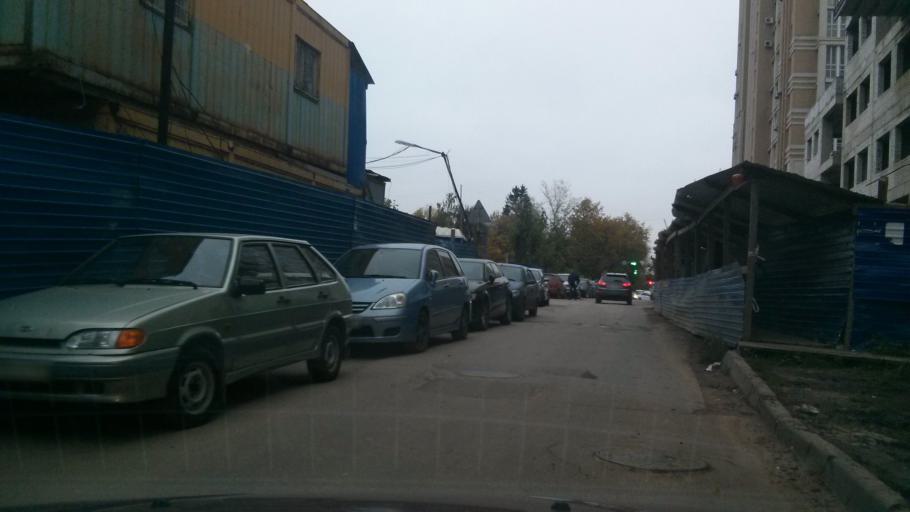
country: RU
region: Nizjnij Novgorod
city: Nizhniy Novgorod
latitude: 56.3130
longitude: 44.0024
